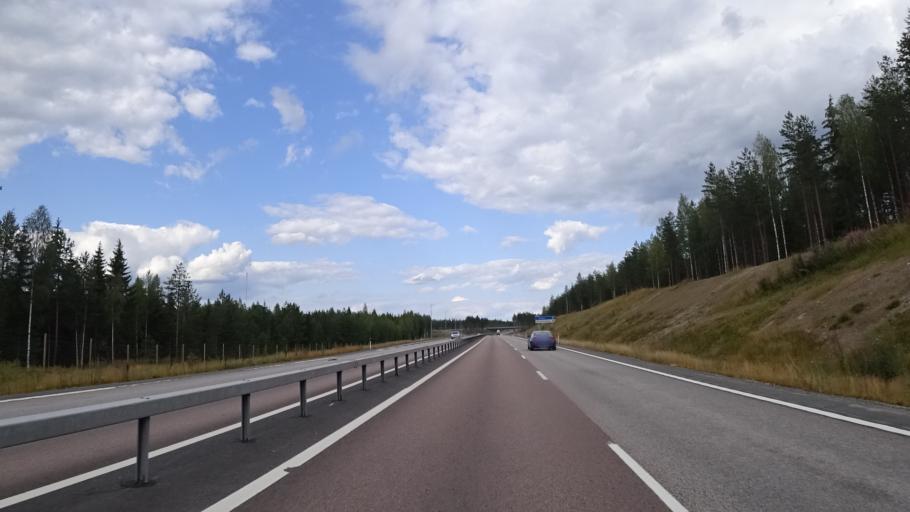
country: FI
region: South Karelia
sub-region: Lappeenranta
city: Lemi
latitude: 60.9704
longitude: 27.8637
